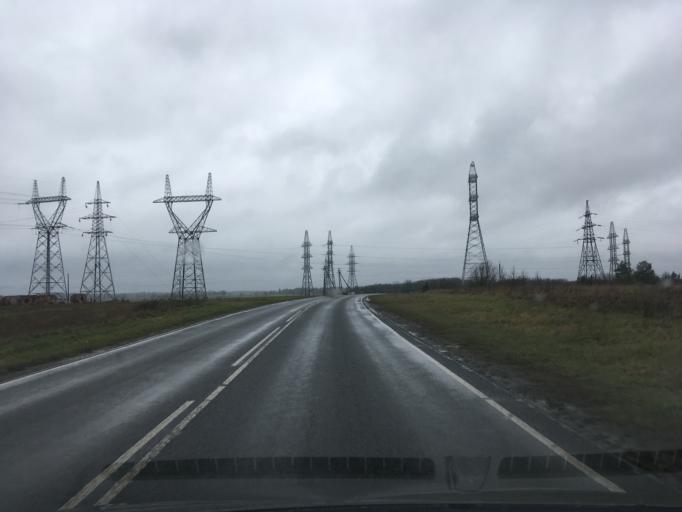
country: EE
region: Laeaene
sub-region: Lihula vald
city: Lihula
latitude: 58.6761
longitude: 23.8182
